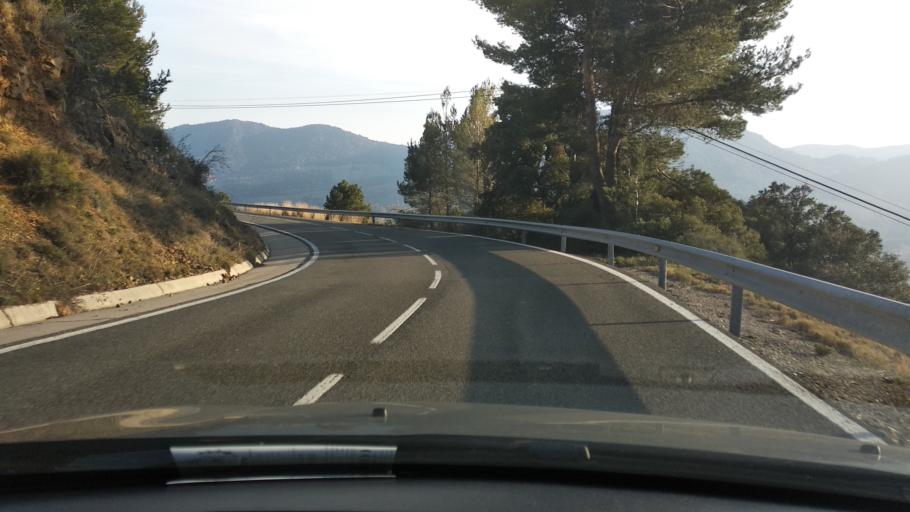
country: ES
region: Catalonia
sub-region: Provincia de Tarragona
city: Alforja
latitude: 41.2191
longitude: 0.9507
